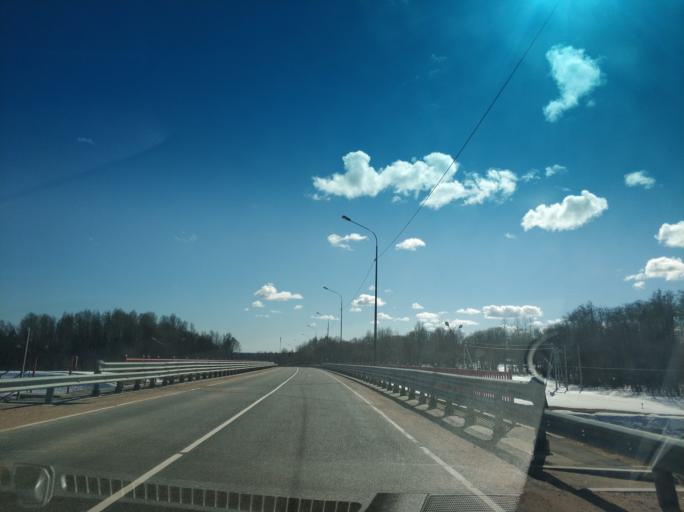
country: RU
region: Leningrad
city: Sosnovo
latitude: 60.4341
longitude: 30.2360
